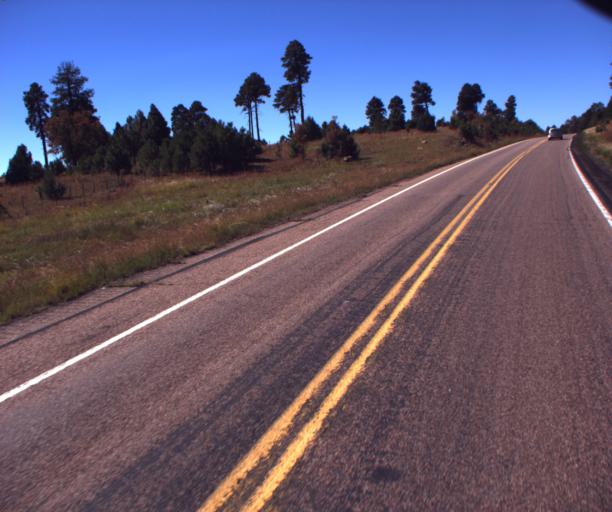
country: US
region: Arizona
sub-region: Navajo County
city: Heber-Overgaard
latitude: 34.3452
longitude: -110.7097
